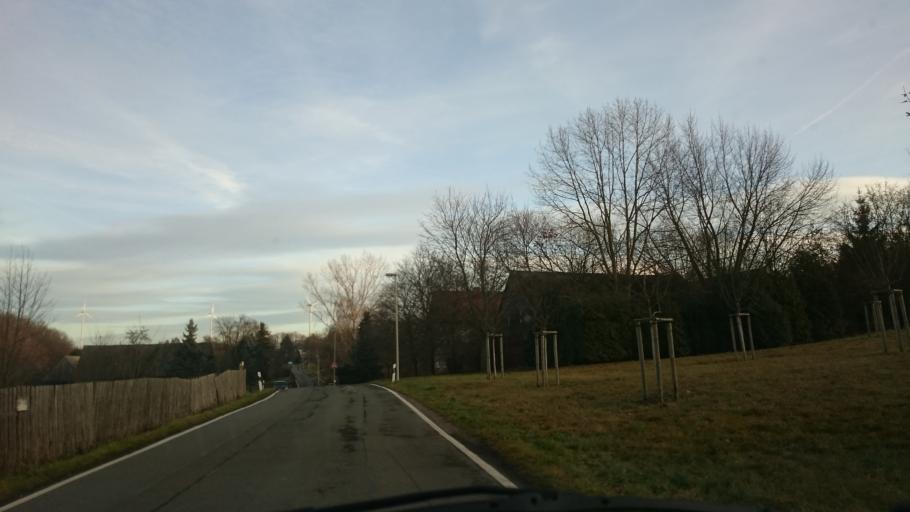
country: DE
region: Saxony
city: Zwickau
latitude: 50.7381
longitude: 12.5194
